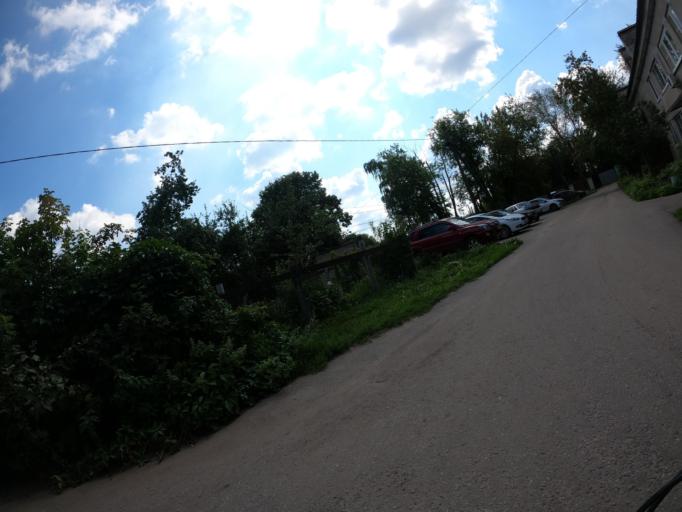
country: RU
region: Moskovskaya
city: Lopatinskiy
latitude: 55.3128
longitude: 38.7089
